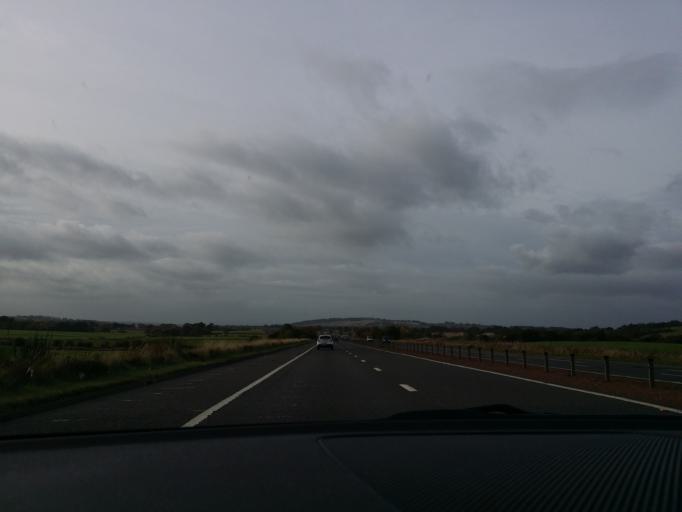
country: GB
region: Scotland
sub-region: West Lothian
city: Broxburn
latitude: 55.9807
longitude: -3.5040
